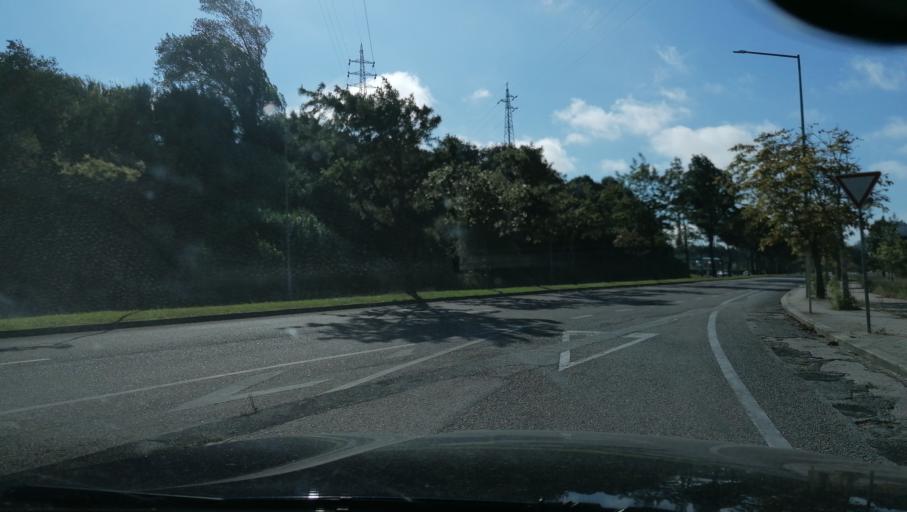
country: PT
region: Aveiro
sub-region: Aveiro
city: Aveiro
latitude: 40.6366
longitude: -8.6371
